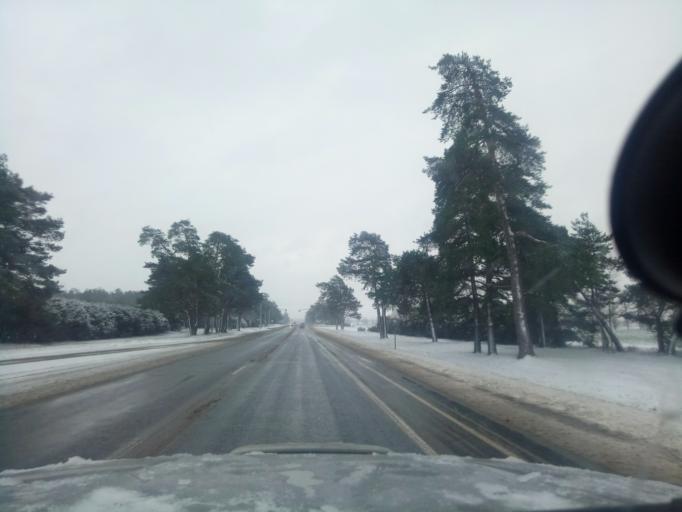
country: BY
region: Minsk
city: Nyasvizh
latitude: 53.2485
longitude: 26.6232
